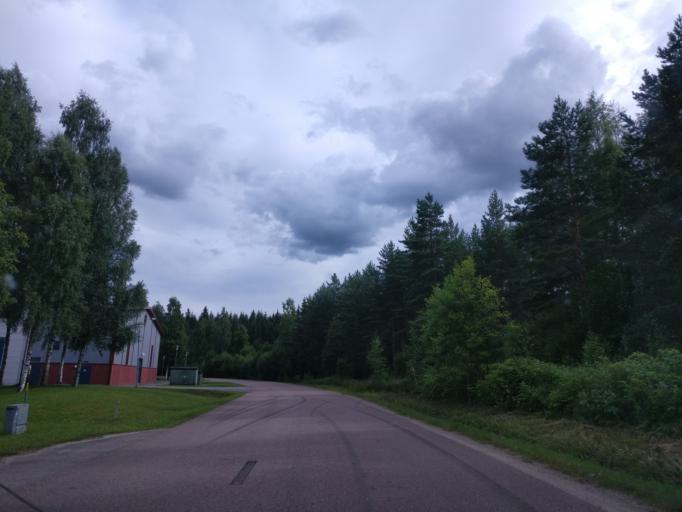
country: SE
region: Vaermland
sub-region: Hagfors Kommun
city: Ekshaerad
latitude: 60.1632
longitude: 13.4985
